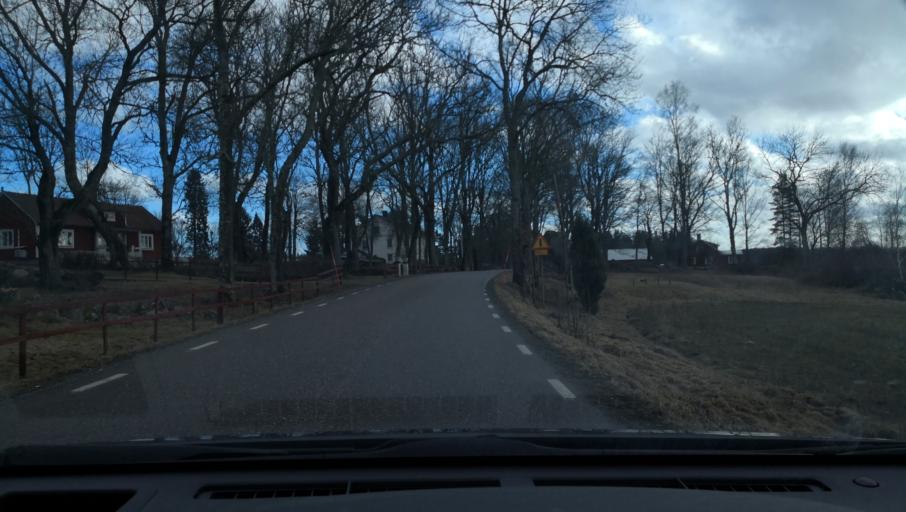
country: SE
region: OErebro
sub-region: Lindesbergs Kommun
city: Fellingsbro
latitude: 59.3475
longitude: 15.6860
